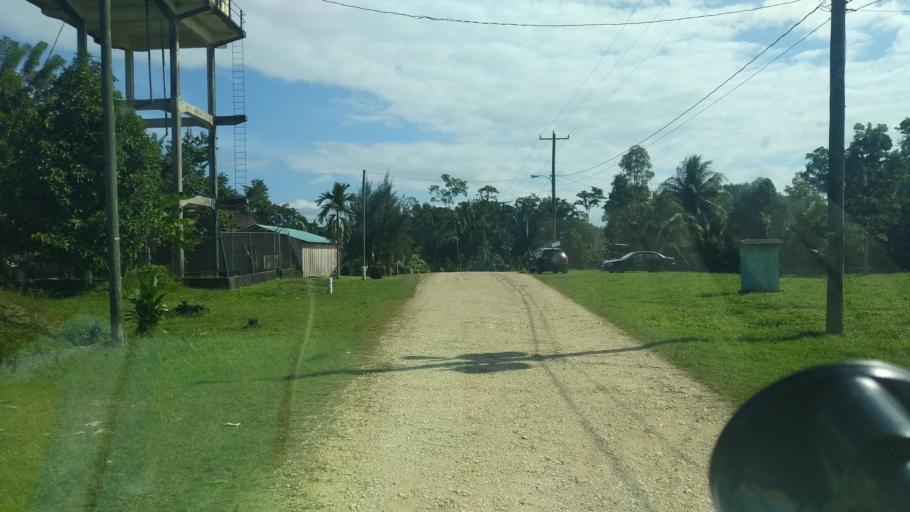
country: BZ
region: Toledo
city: Punta Gorda
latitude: 16.2163
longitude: -88.9045
